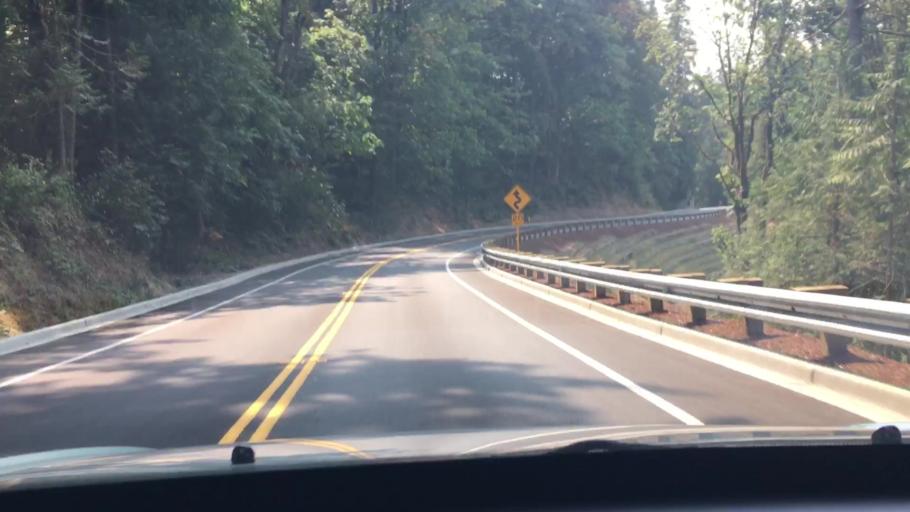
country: US
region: Washington
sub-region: King County
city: City of Sammamish
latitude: 47.5780
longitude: -122.0576
